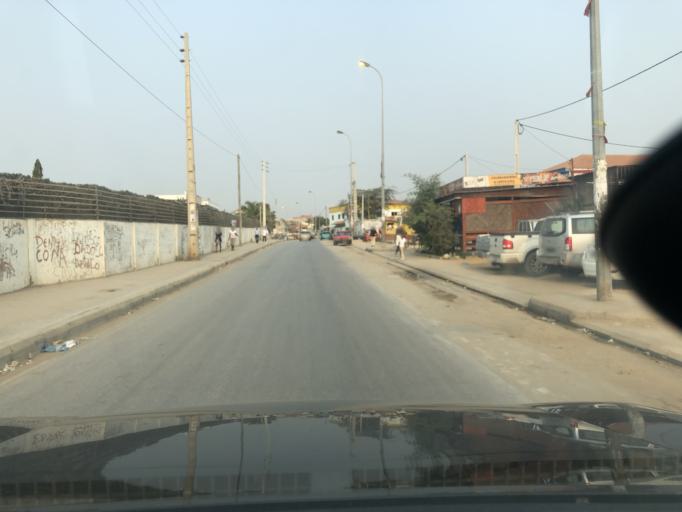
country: AO
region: Luanda
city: Luanda
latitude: -8.8797
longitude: 13.1901
